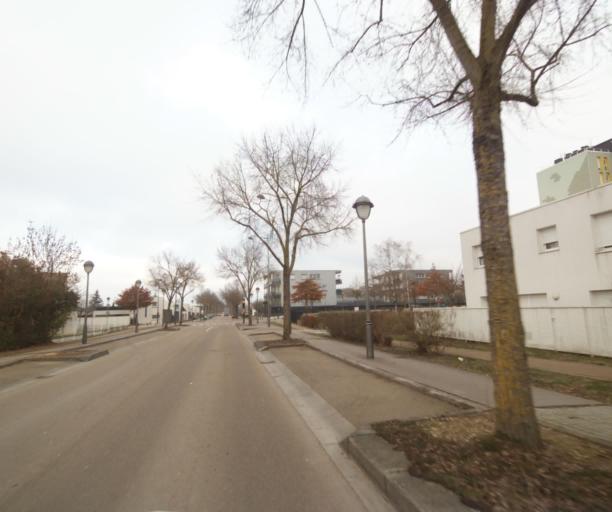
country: FR
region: Champagne-Ardenne
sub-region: Departement de la Haute-Marne
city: Bettancourt-la-Ferree
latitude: 48.6387
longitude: 4.9727
